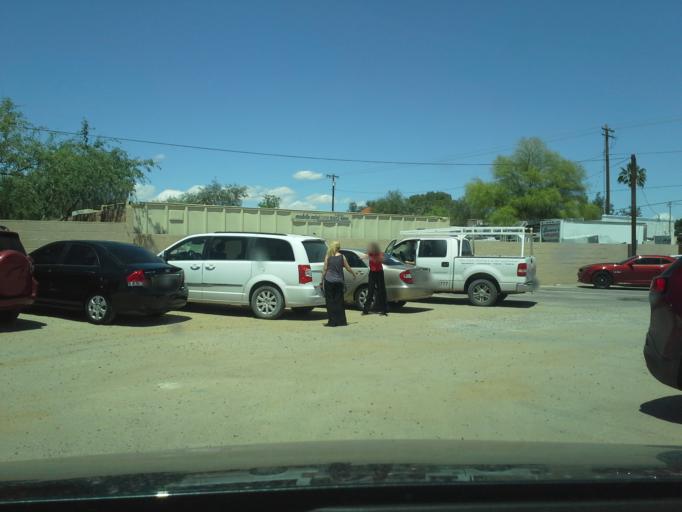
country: US
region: Arizona
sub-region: Pima County
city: Tucson
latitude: 32.2497
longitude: -110.9281
